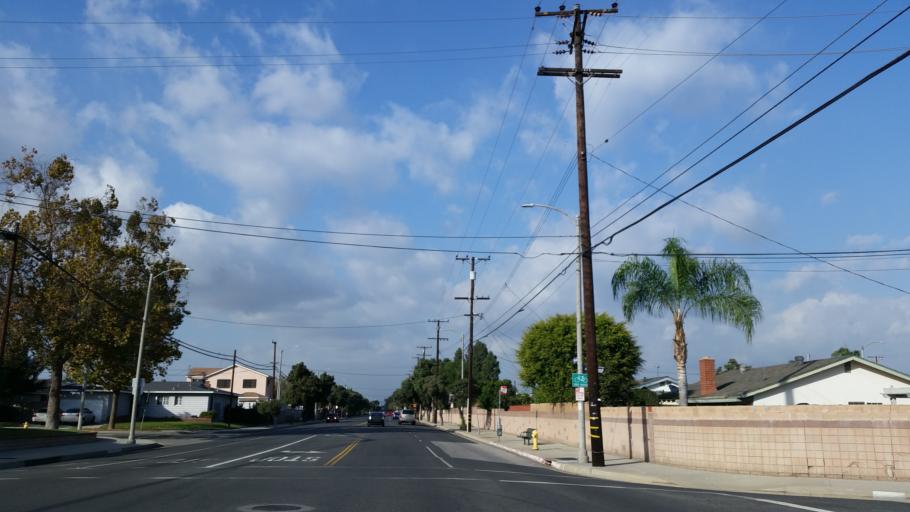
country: US
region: California
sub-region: Los Angeles County
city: Lakewood
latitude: 33.8531
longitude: -118.1083
